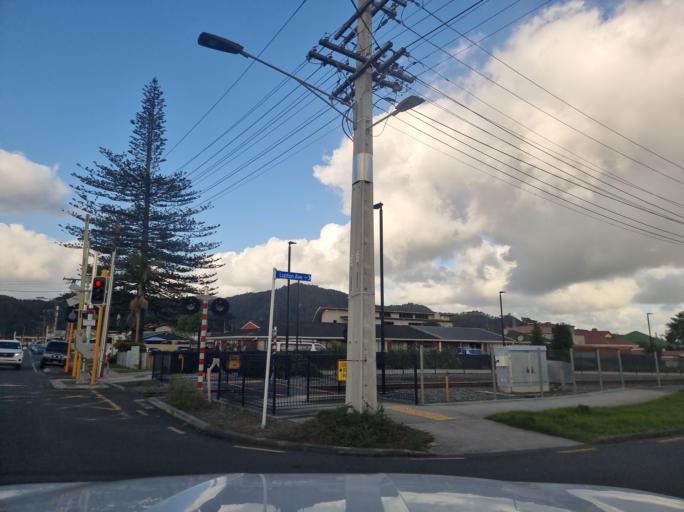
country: NZ
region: Northland
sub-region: Whangarei
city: Whangarei
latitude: -35.7092
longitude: 174.3186
